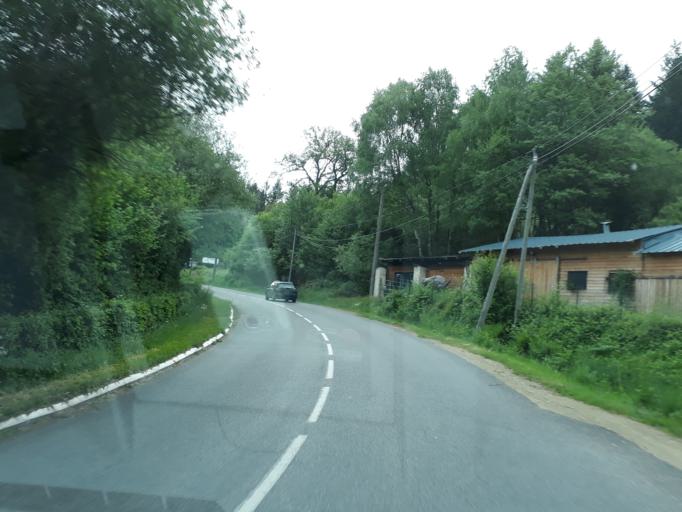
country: FR
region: Limousin
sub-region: Departement de la Haute-Vienne
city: Peyrat-le-Chateau
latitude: 45.8074
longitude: 1.8220
